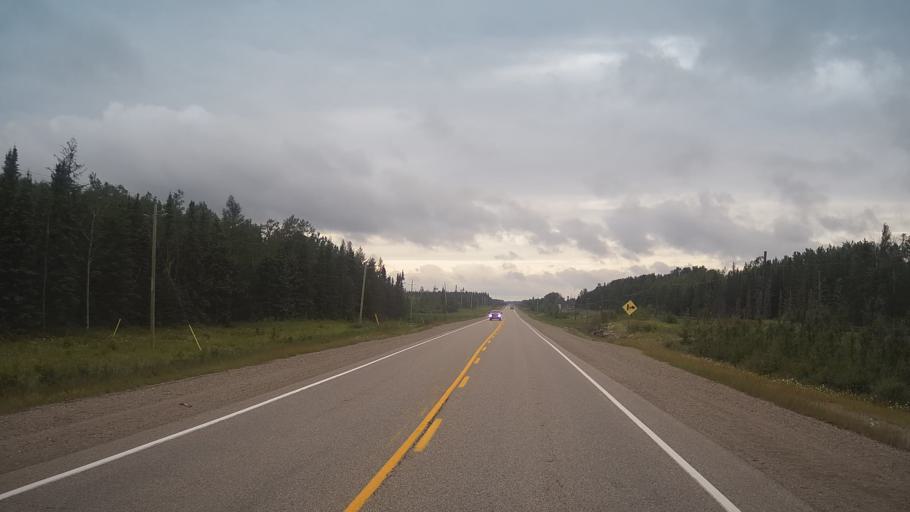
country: CA
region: Ontario
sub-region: Thunder Bay District
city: Thunder Bay
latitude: 48.8434
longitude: -89.9425
